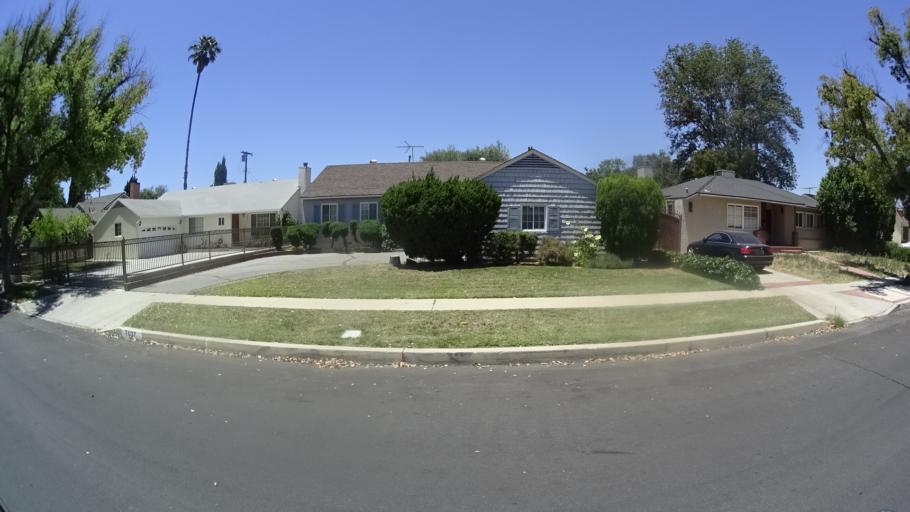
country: US
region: California
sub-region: Los Angeles County
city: Northridge
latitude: 34.1986
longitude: -118.5153
